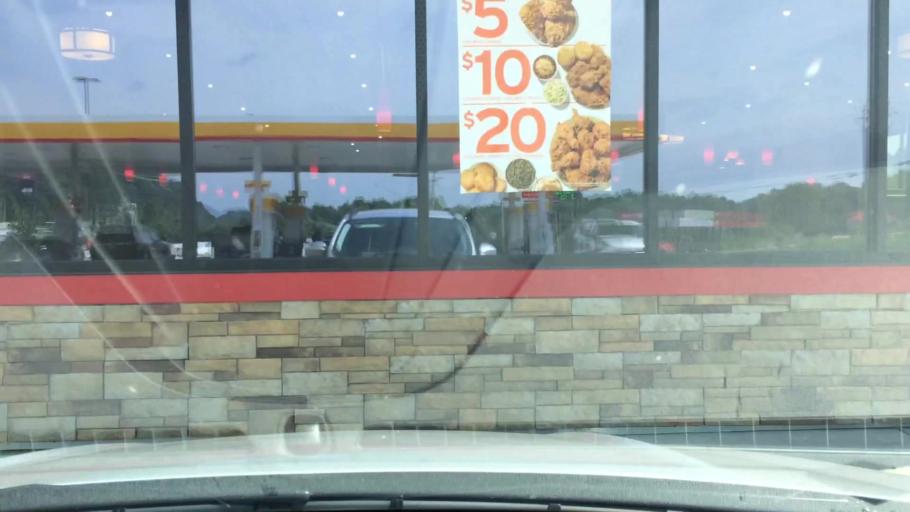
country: US
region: Tennessee
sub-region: Campbell County
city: Jacksboro
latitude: 36.3765
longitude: -84.2472
